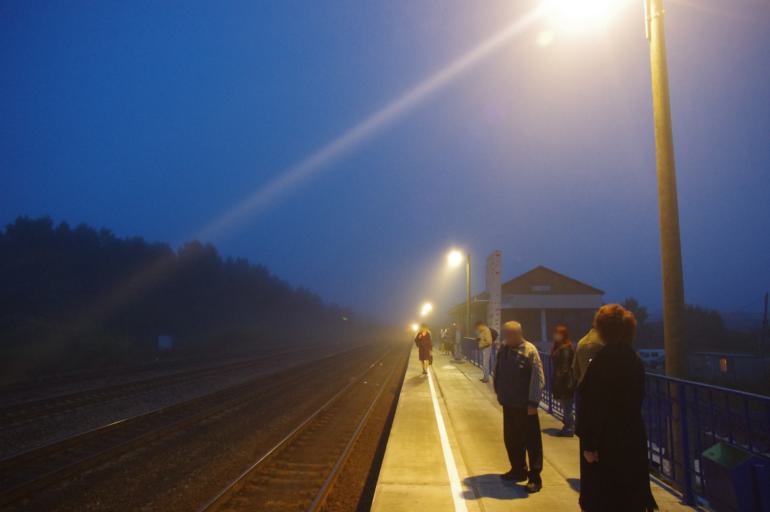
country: RU
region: Jaroslavl
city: Borok
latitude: 57.9316
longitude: 38.2397
